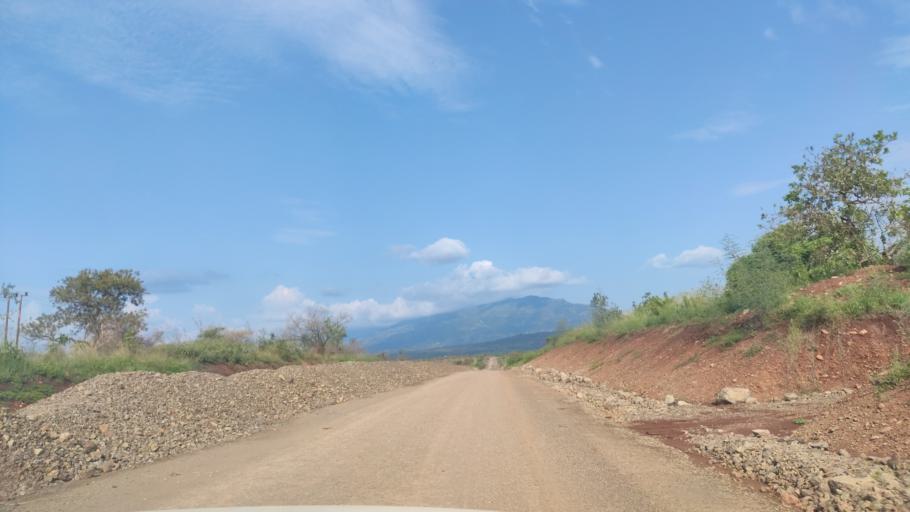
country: ET
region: Southern Nations, Nationalities, and People's Region
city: Felege Neway
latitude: 6.4246
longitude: 37.2459
